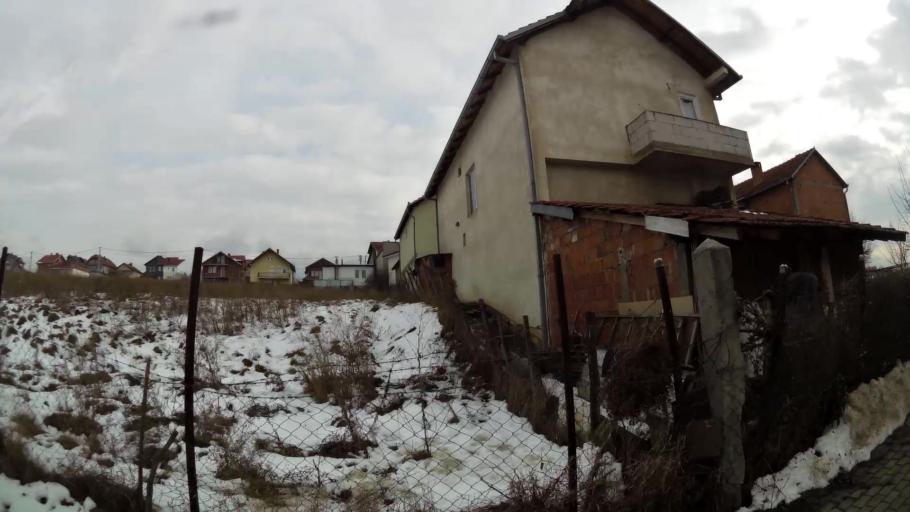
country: XK
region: Pristina
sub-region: Komuna e Prishtines
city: Pristina
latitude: 42.6855
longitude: 21.1626
